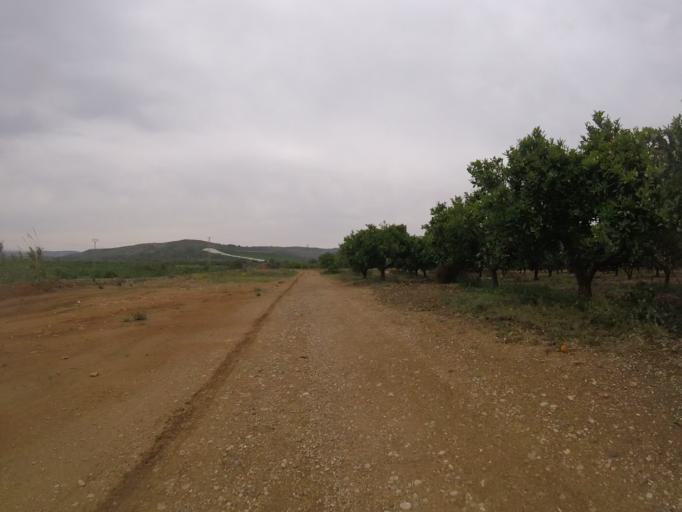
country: ES
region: Valencia
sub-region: Provincia de Castello
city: Alcoceber
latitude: 40.2662
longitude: 0.2576
